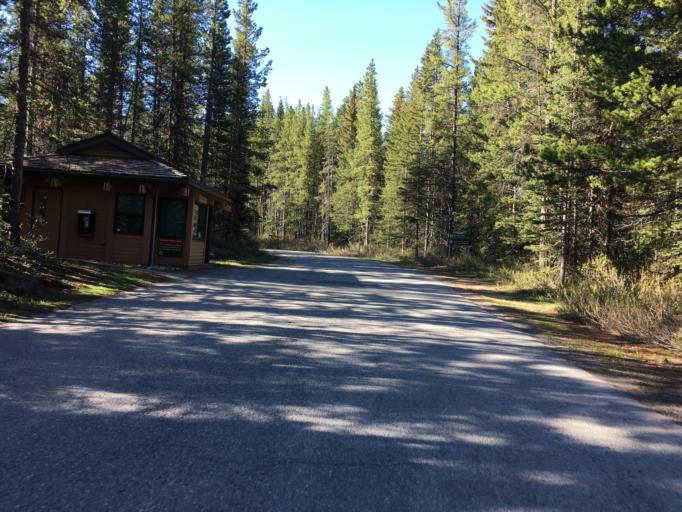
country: CA
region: Alberta
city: Canmore
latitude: 50.6366
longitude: -115.1044
